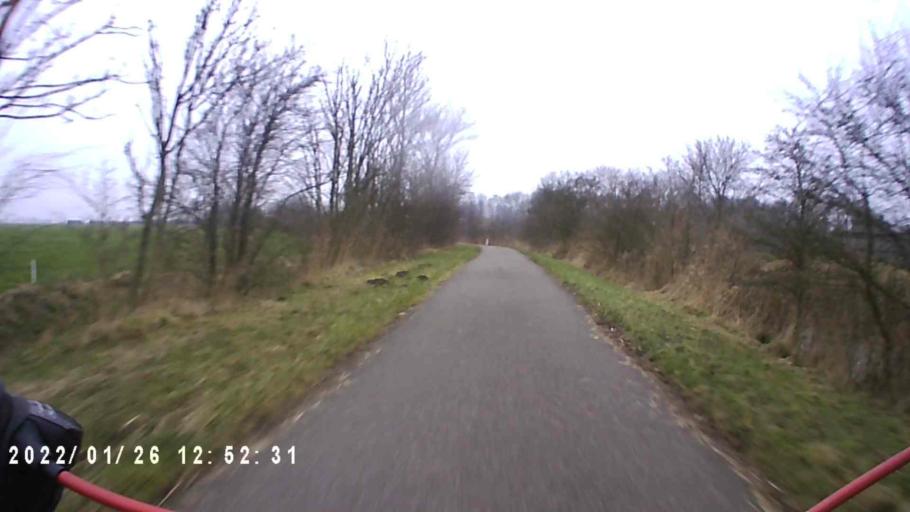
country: NL
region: Groningen
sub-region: Gemeente Winsum
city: Winsum
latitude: 53.3390
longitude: 6.4934
